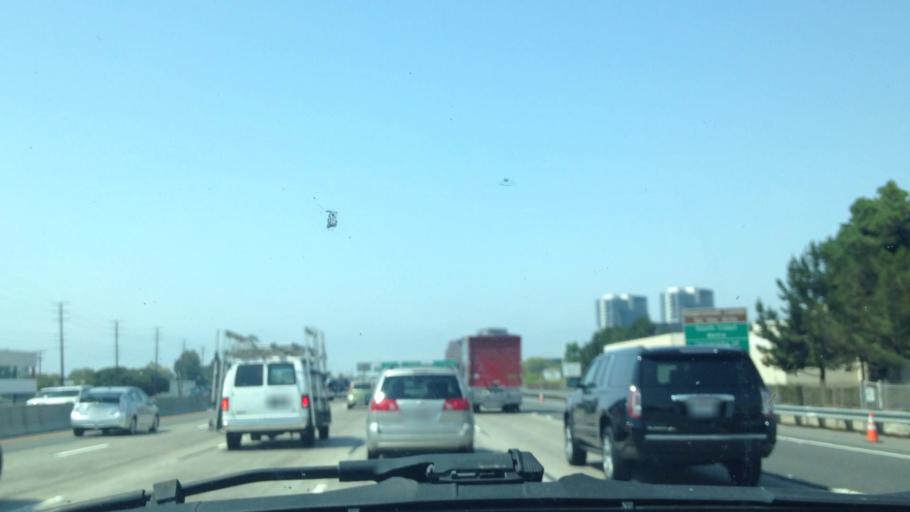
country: US
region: California
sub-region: Orange County
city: Santa Ana
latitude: 33.7035
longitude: -117.8574
